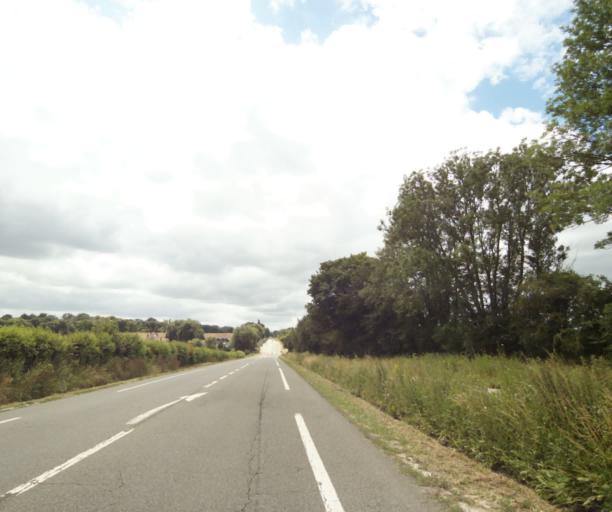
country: FR
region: Ile-de-France
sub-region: Departement des Yvelines
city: Bailly
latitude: 48.8208
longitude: 2.0817
